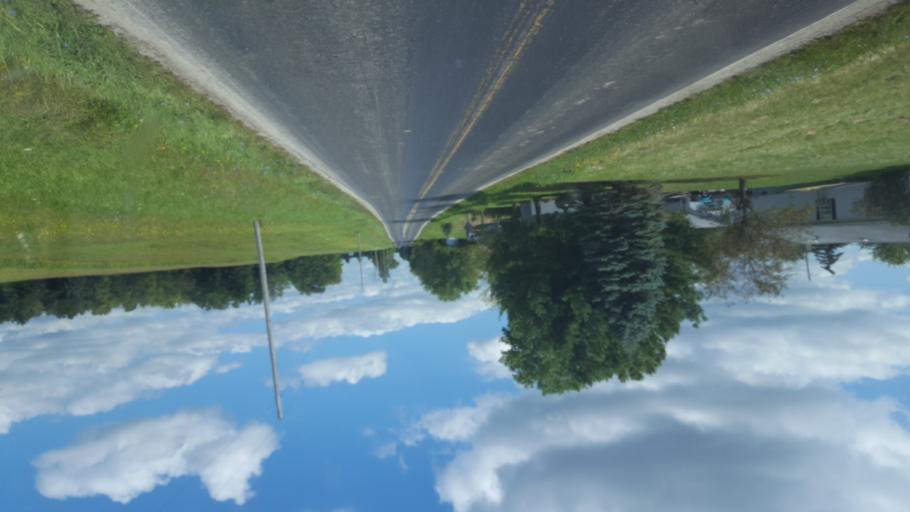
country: US
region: Ohio
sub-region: Wayne County
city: West Salem
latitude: 40.9920
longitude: -82.1884
